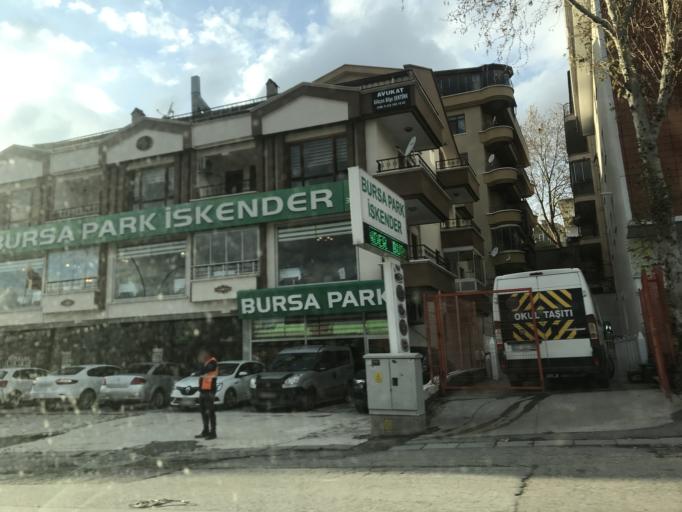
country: TR
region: Ankara
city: Mamak
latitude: 39.9689
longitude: 32.8755
